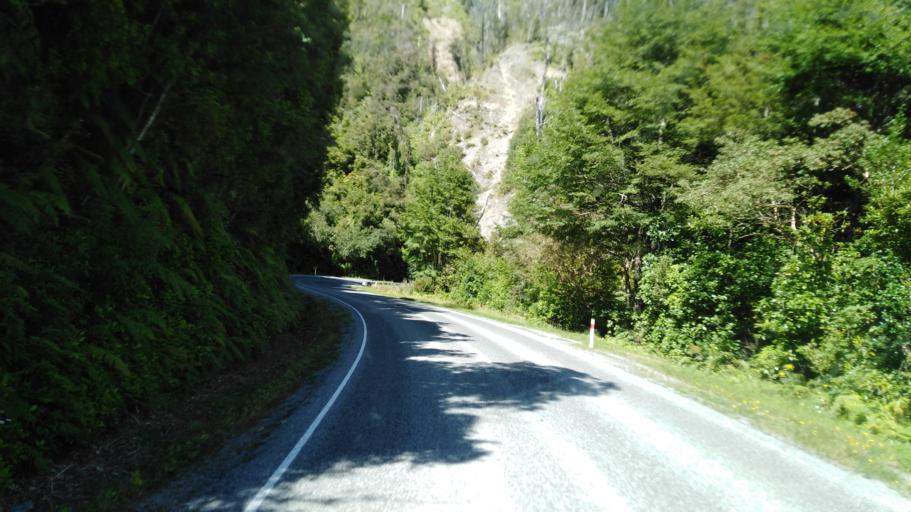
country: NZ
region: West Coast
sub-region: Buller District
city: Westport
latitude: -41.4946
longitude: 172.0480
